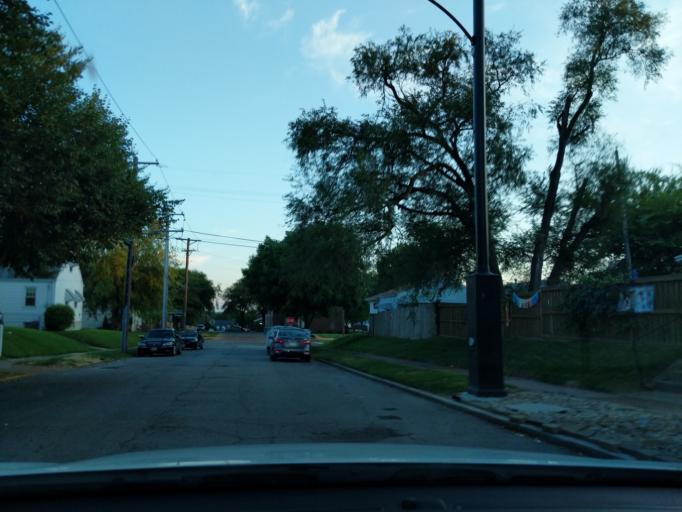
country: US
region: Missouri
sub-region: Saint Louis County
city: Maplewood
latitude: 38.6073
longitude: -90.2856
